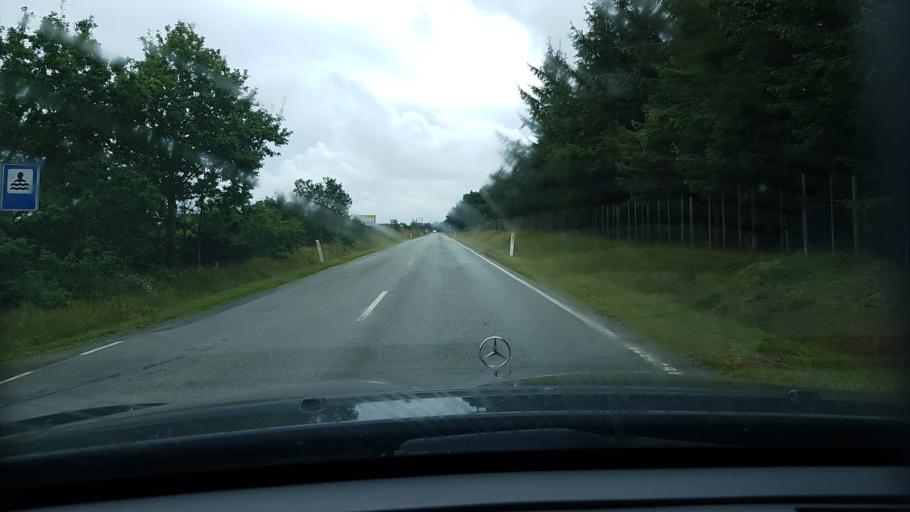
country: DK
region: North Denmark
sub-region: Alborg Kommune
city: Hals
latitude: 56.8297
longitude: 10.2685
